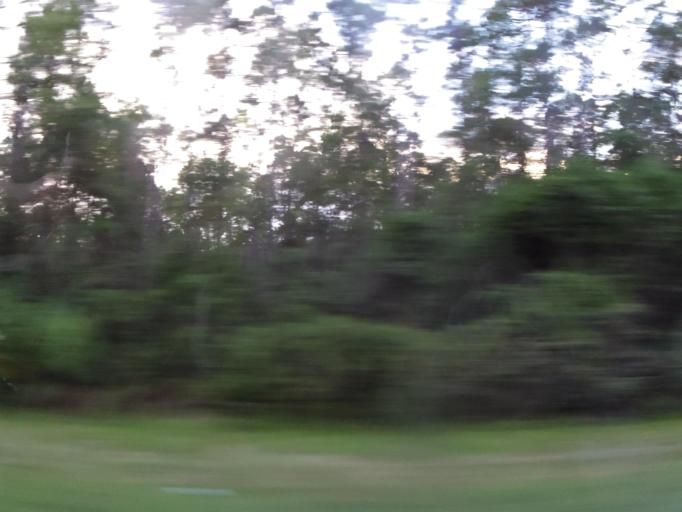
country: US
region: Georgia
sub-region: Echols County
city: Statenville
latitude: 30.7237
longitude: -83.0757
